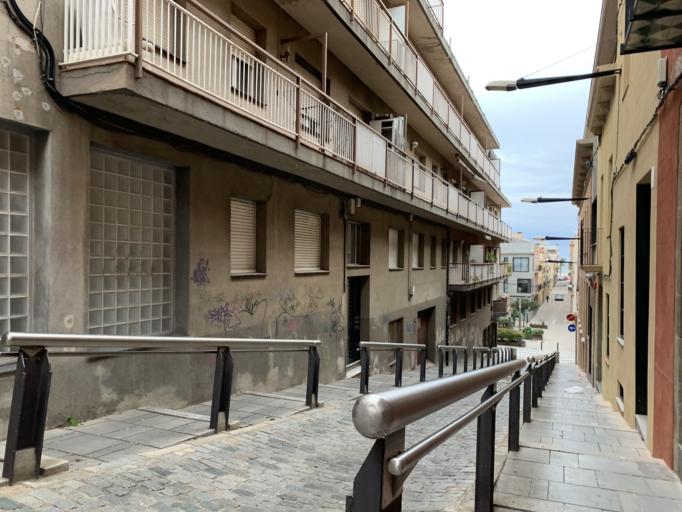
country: ES
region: Catalonia
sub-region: Provincia de Barcelona
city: Mataro
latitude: 41.5389
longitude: 2.4473
